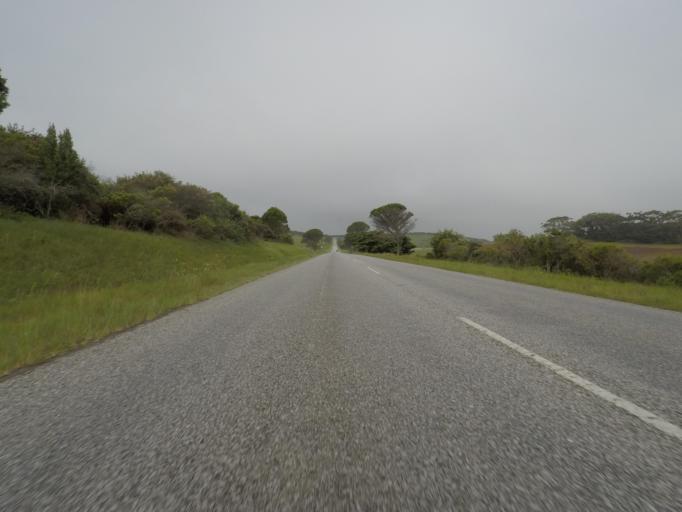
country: ZA
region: Eastern Cape
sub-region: Cacadu District Municipality
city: Port Alfred
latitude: -33.6060
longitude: 26.8300
